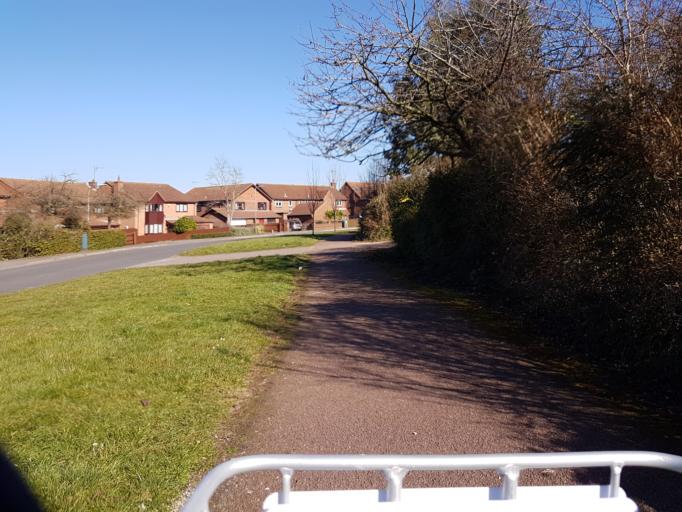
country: GB
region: England
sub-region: Buckinghamshire
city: Newton Longville
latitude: 52.0058
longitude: -0.7639
